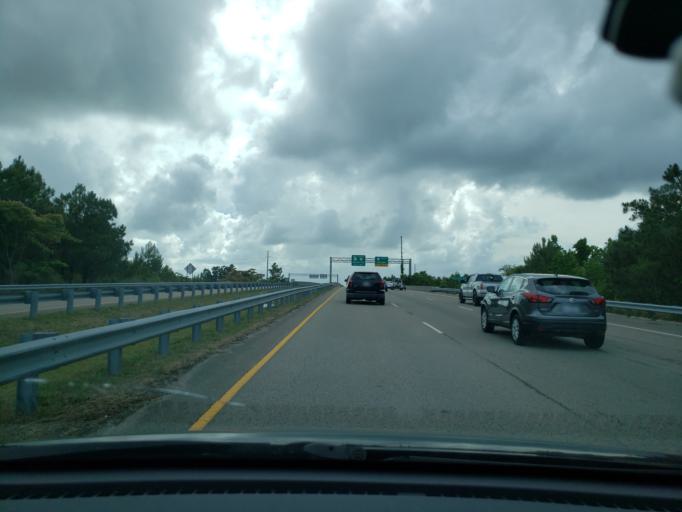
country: US
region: North Carolina
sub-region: New Hanover County
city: Wrightsboro
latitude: 34.2605
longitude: -77.9269
